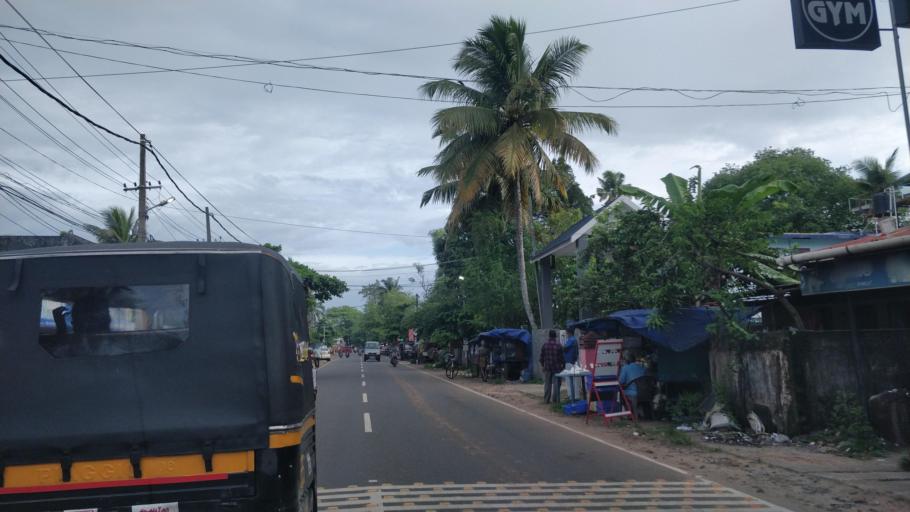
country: IN
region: Kerala
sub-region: Alappuzha
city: Alleppey
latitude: 9.5193
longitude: 76.3390
